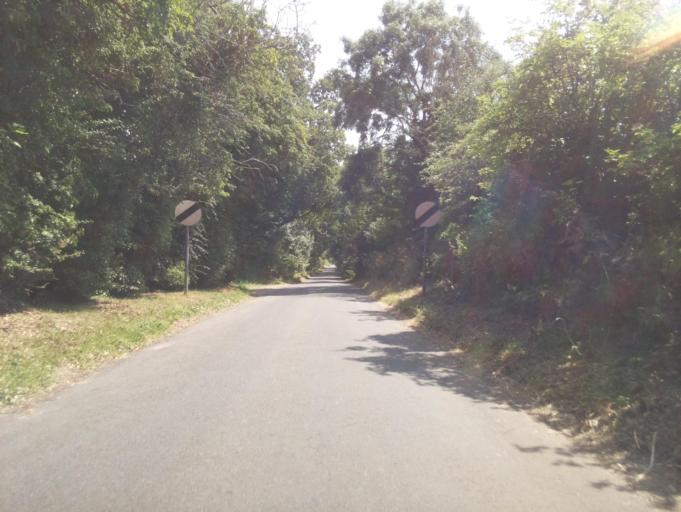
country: GB
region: England
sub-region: Gloucestershire
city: Donnington
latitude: 51.9511
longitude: -1.7174
